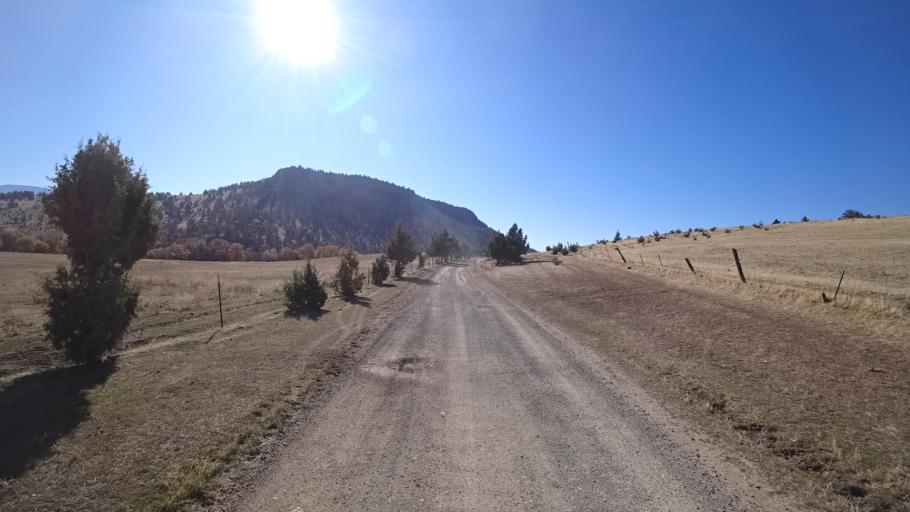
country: US
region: California
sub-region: Siskiyou County
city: Montague
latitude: 41.7417
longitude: -122.3335
